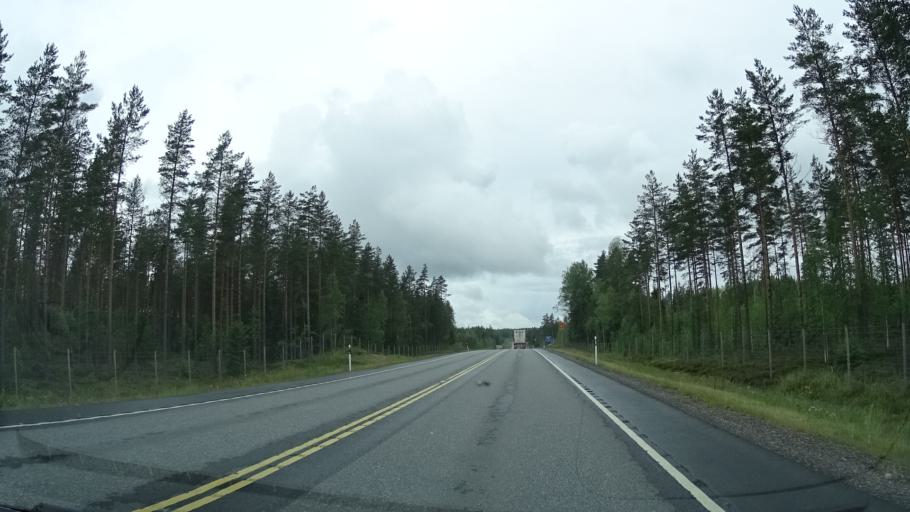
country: FI
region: Uusimaa
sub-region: Helsinki
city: Karkkila
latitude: 60.5881
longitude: 24.1188
